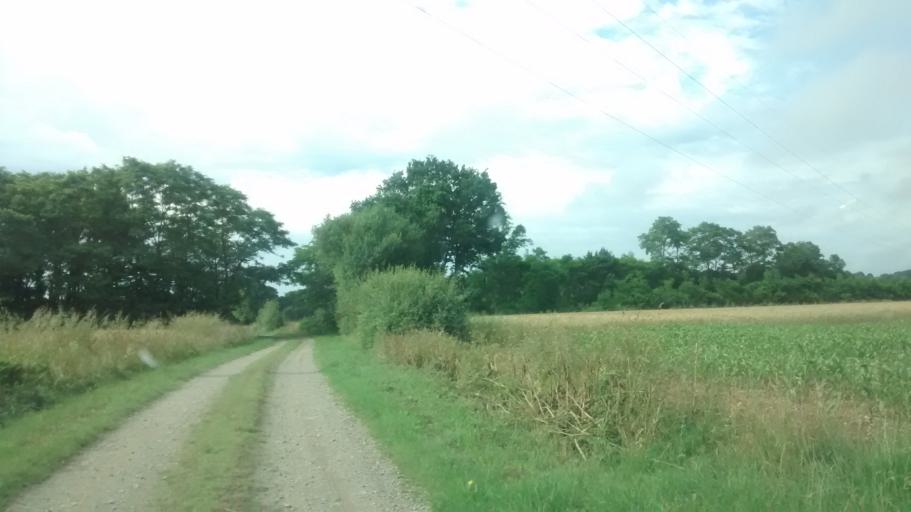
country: FR
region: Brittany
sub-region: Departement d'Ille-et-Vilaine
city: Plechatel
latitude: 47.8361
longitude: -1.7465
